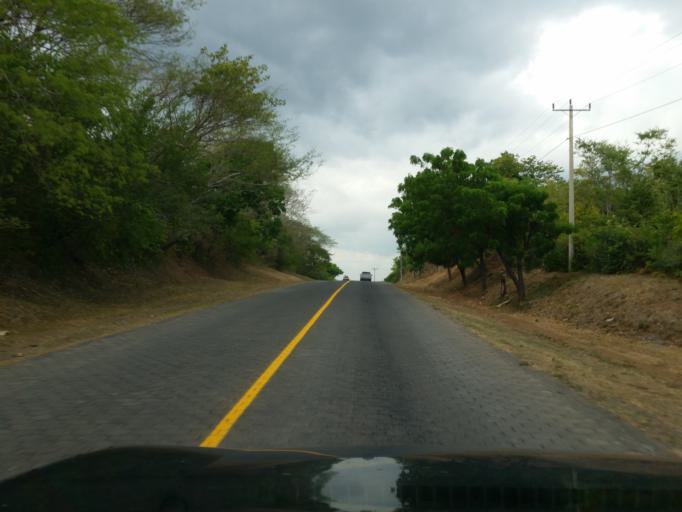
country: NI
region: Managua
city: San Rafael del Sur
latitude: 11.8787
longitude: -86.5153
